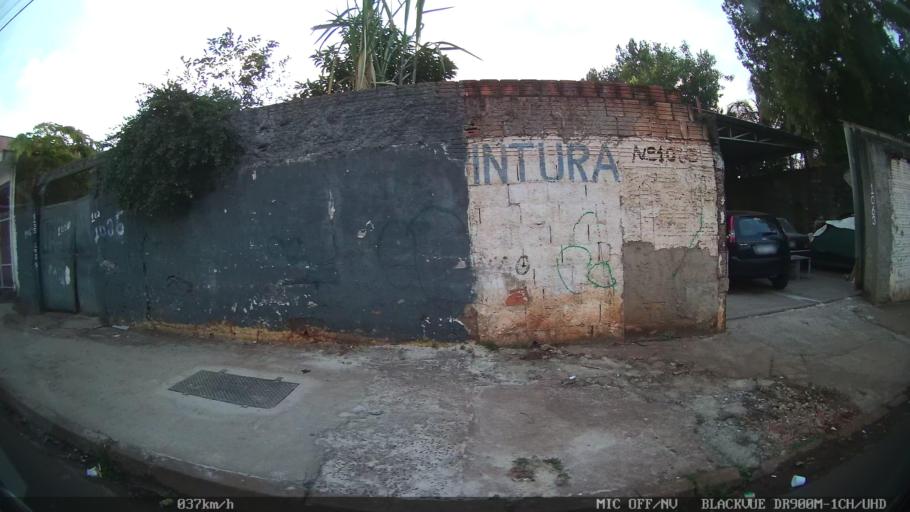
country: BR
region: Sao Paulo
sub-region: Ribeirao Preto
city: Ribeirao Preto
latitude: -21.1502
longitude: -47.8261
